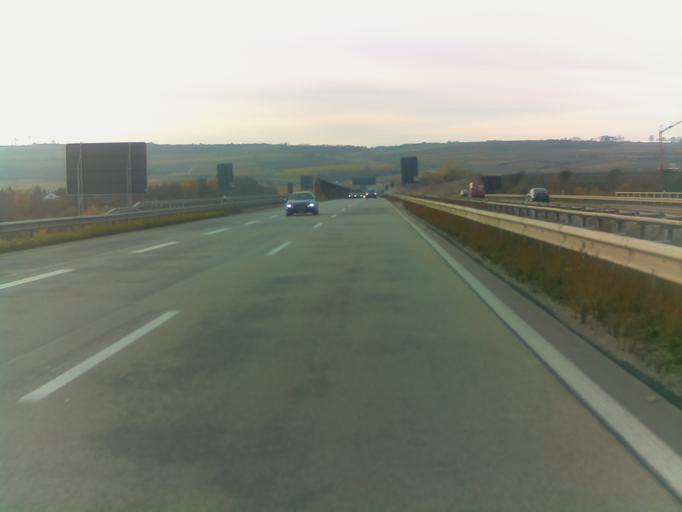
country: DE
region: Rheinland-Pfalz
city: Grunstadt
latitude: 49.5530
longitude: 8.1750
